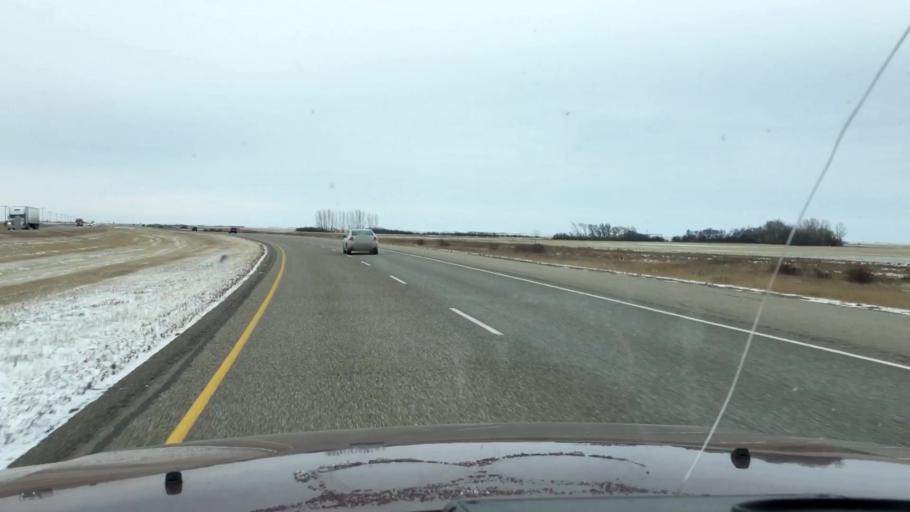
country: CA
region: Saskatchewan
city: Watrous
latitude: 51.1444
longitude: -105.9062
